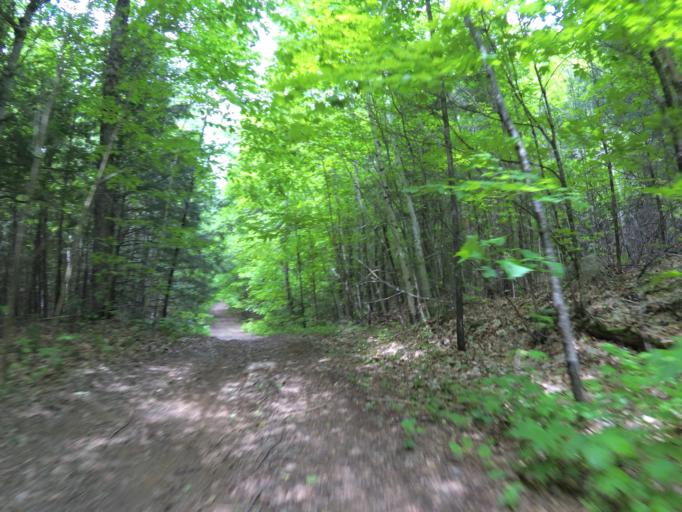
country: CA
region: Ontario
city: Renfrew
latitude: 45.0574
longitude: -76.8663
